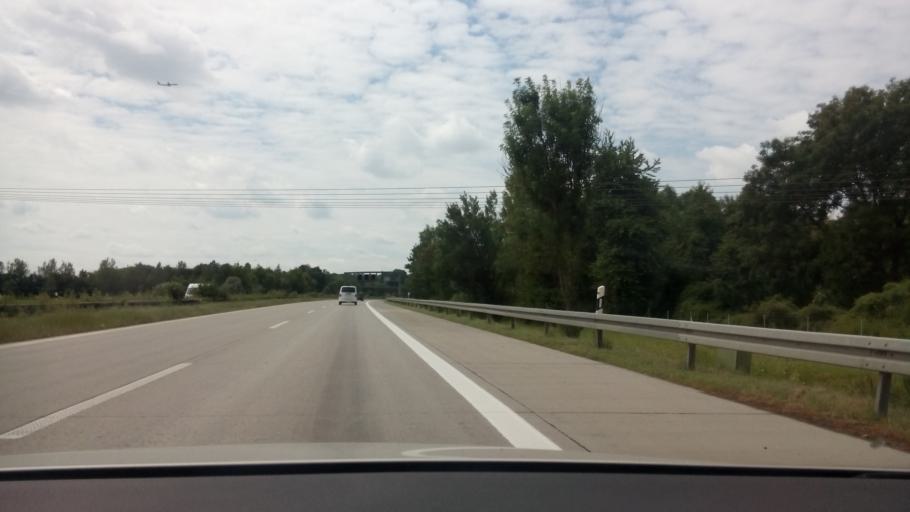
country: DE
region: Bavaria
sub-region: Upper Bavaria
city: Hallbergmoos
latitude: 48.3550
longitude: 11.7306
